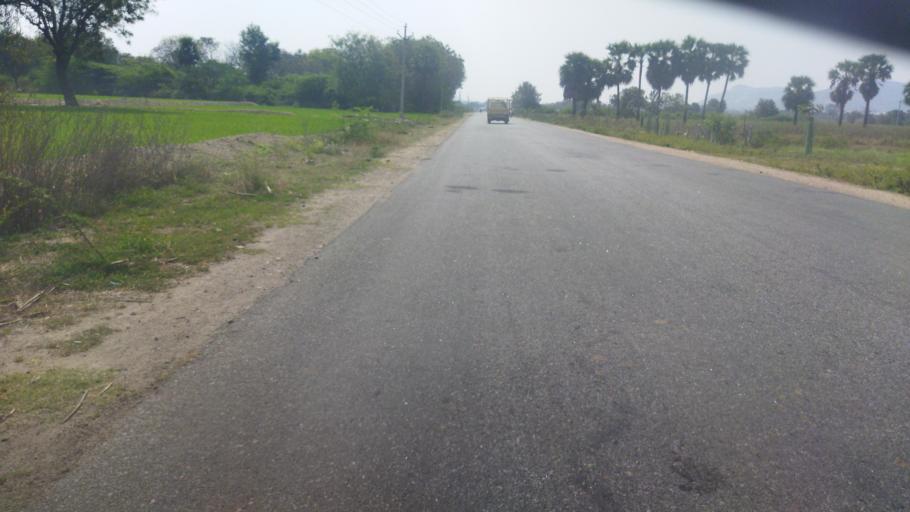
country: IN
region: Telangana
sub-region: Nalgonda
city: Nalgonda
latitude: 17.0909
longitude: 79.2853
